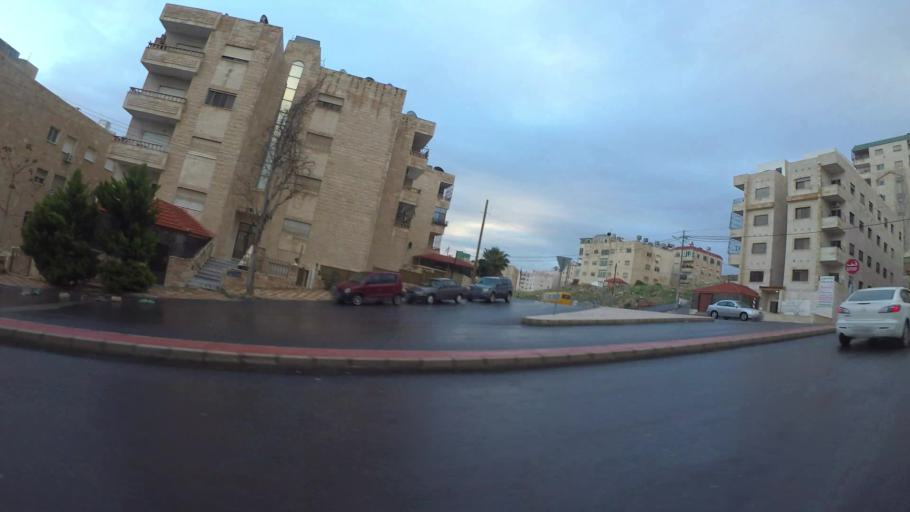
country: JO
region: Amman
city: Amman
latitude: 31.9856
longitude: 35.9161
